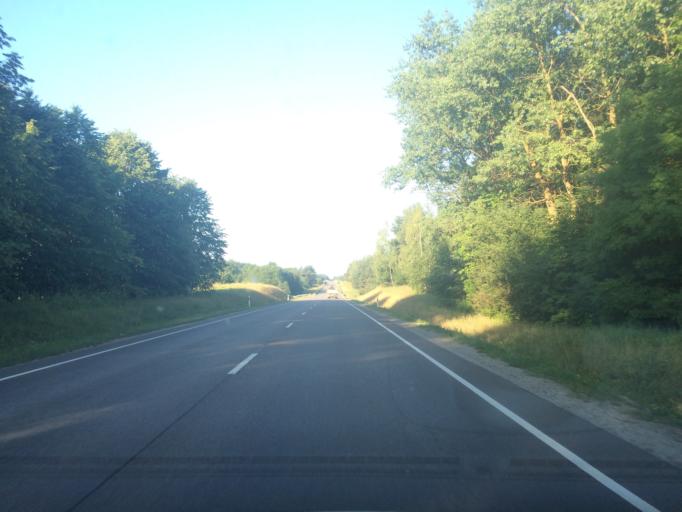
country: LT
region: Vilnius County
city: Ukmerge
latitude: 55.2968
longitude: 24.8517
